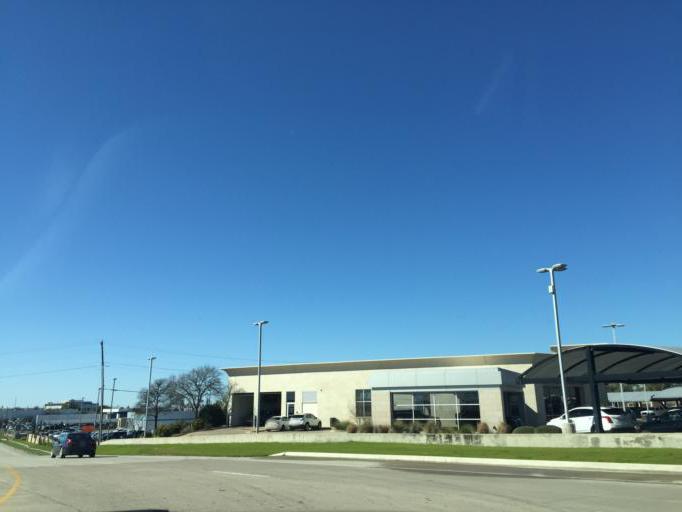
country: US
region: Texas
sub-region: Parker County
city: Hudson Oaks
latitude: 32.7556
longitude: -97.6992
